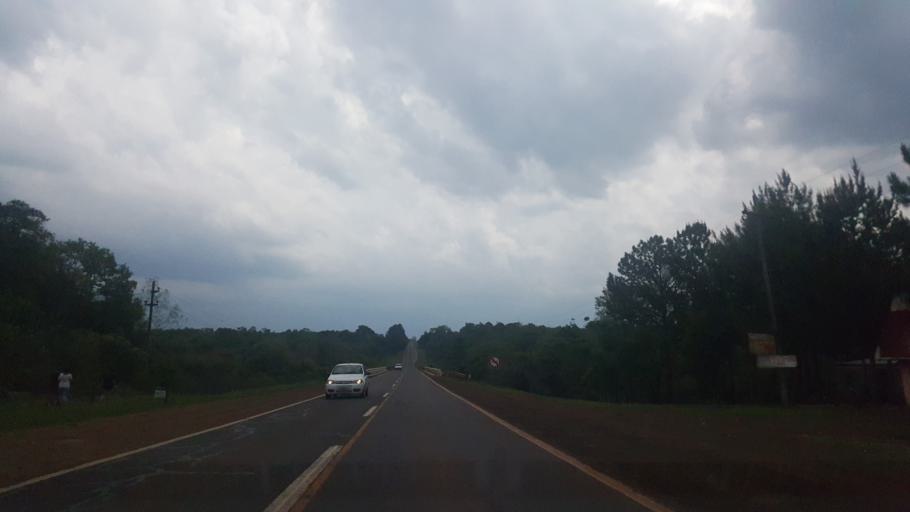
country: AR
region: Misiones
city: Santo Pipo
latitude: -27.1201
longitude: -55.3720
